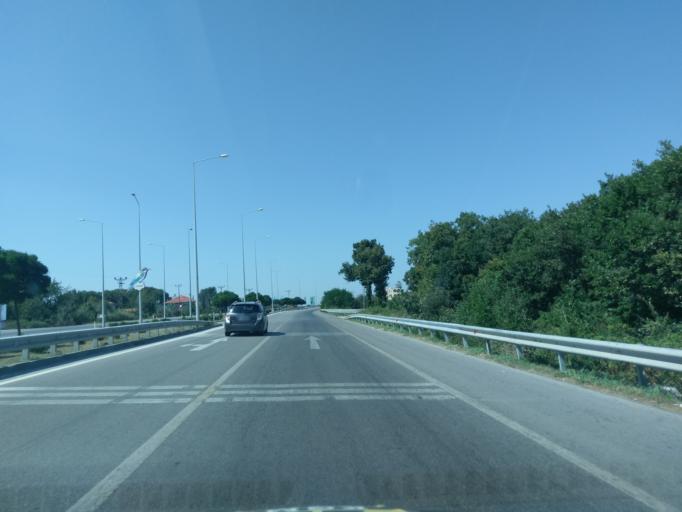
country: TR
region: Samsun
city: Bafra
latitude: 41.5281
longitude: 35.9540
